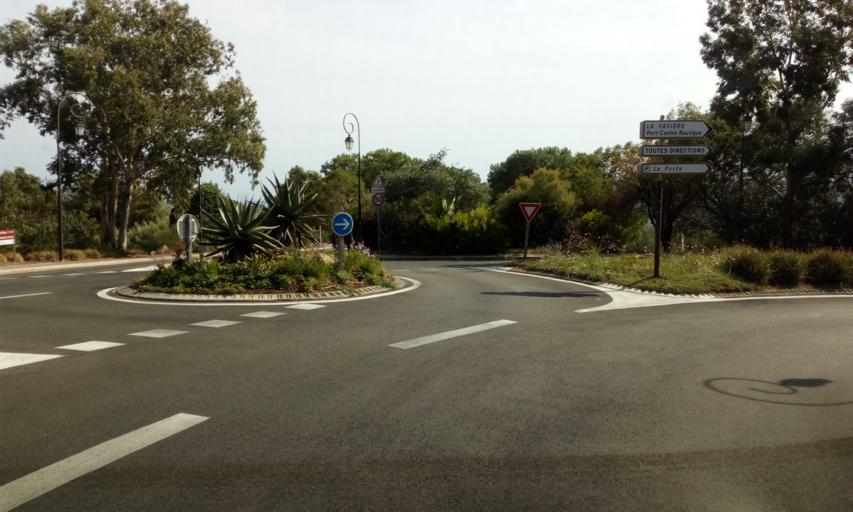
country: FR
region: Provence-Alpes-Cote d'Azur
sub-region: Departement du Var
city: Bormes-les-Mimosas
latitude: 43.1494
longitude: 6.3469
